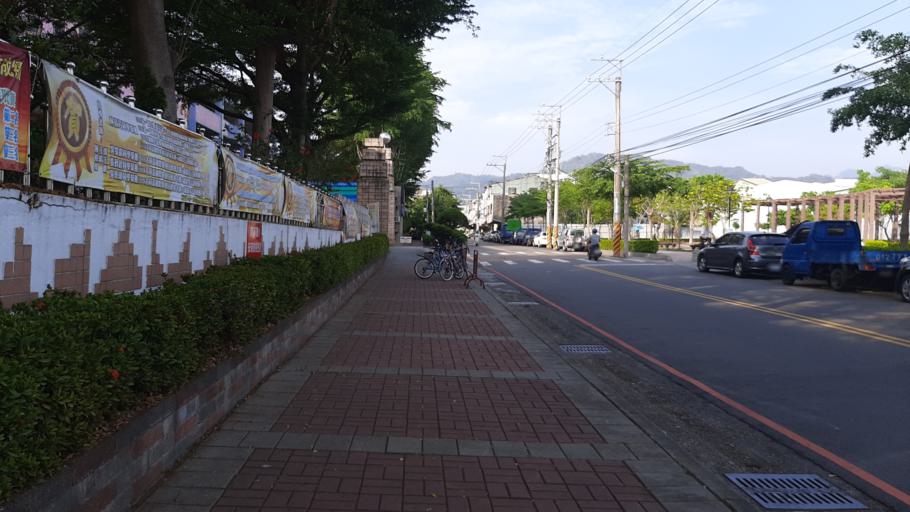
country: TW
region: Taiwan
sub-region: Taichung City
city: Taichung
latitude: 24.1237
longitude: 120.7244
